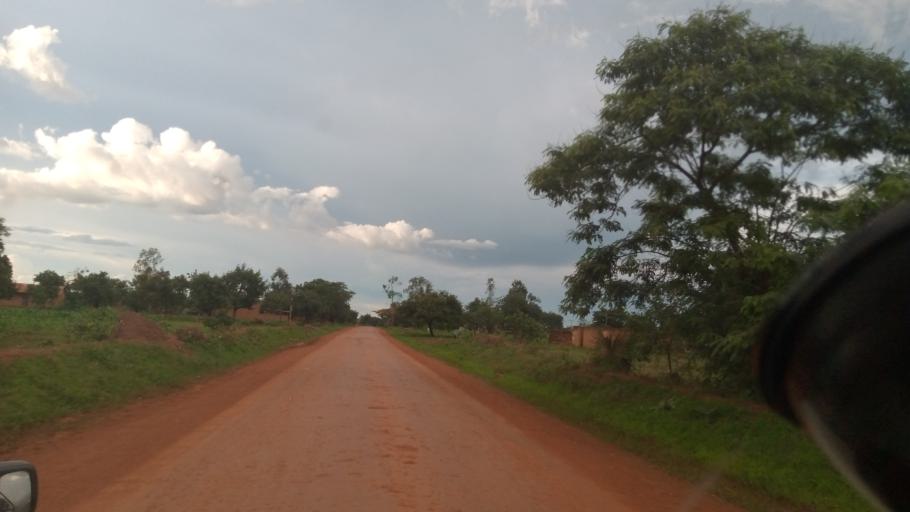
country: UG
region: Northern Region
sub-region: Kole District
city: Kole
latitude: 2.3923
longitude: 32.9337
